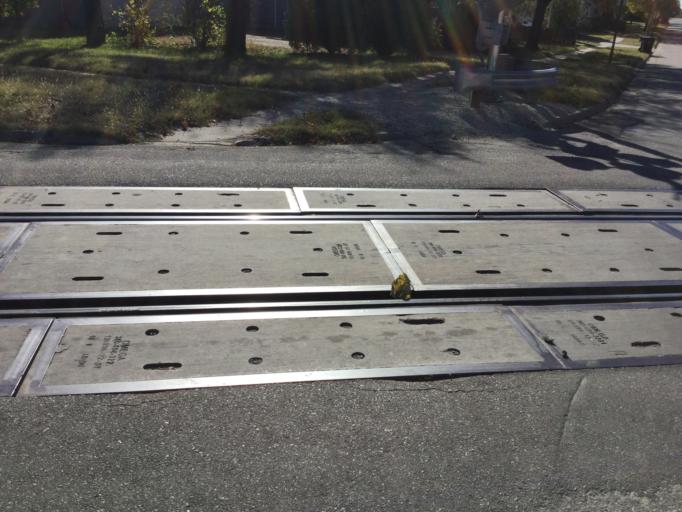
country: US
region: Kansas
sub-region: Harvey County
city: Newton
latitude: 38.0523
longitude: -97.3353
